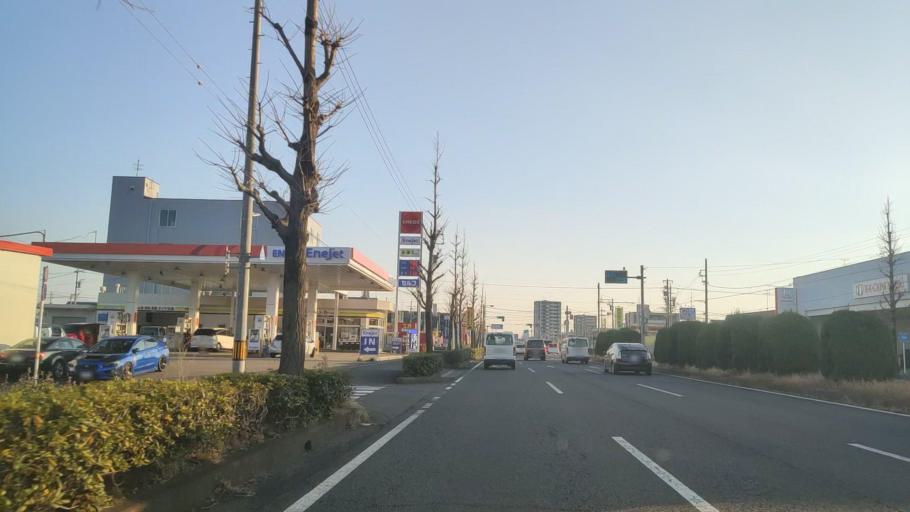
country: JP
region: Gifu
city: Gifu-shi
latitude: 35.4097
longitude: 136.7272
